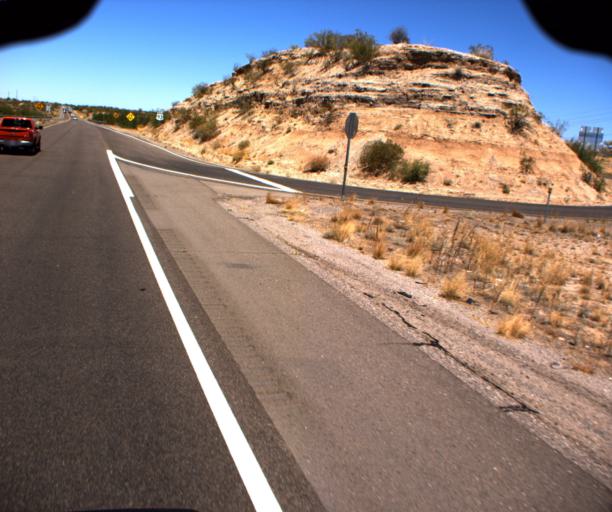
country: US
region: Arizona
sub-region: Maricopa County
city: Wickenburg
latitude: 34.0255
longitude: -112.8092
